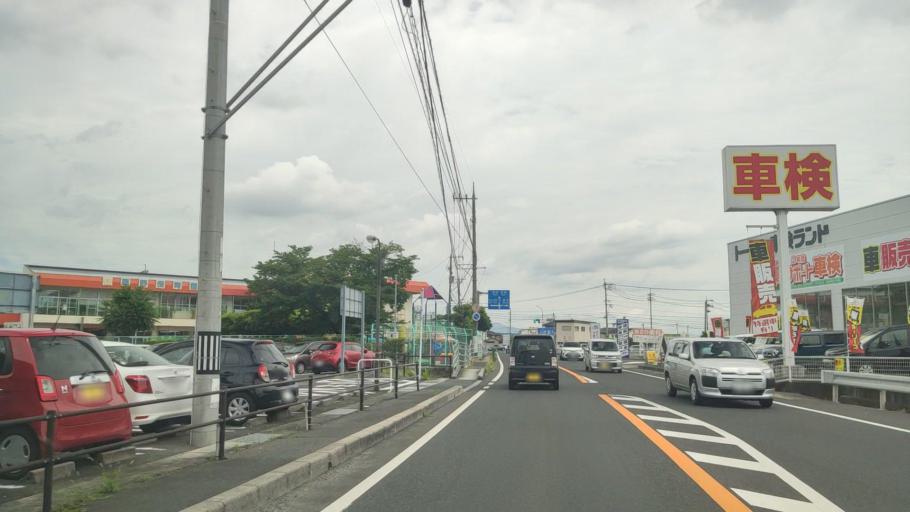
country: JP
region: Okayama
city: Tsuyama
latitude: 35.0720
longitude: 134.0549
